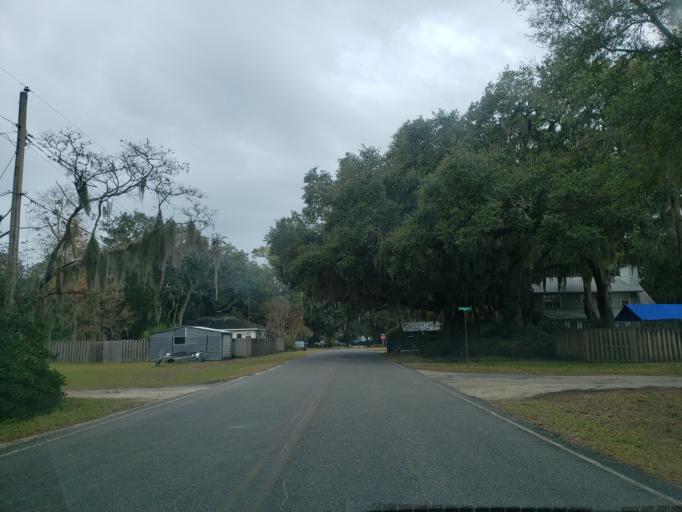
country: US
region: Georgia
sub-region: Chatham County
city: Wilmington Island
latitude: 31.9790
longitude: -80.9973
